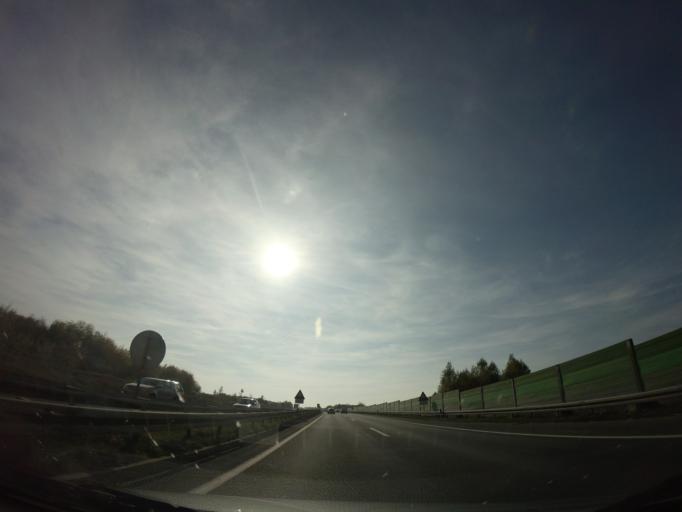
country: HR
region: Grad Zagreb
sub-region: Sesvete
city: Sesvete
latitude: 45.8457
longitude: 16.1437
